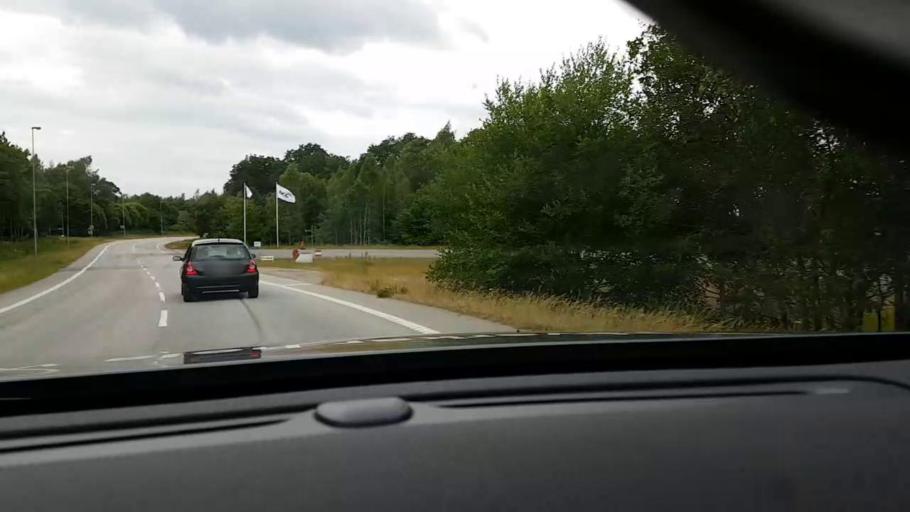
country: SE
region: Skane
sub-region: Hassleholms Kommun
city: Hassleholm
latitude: 56.1723
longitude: 13.7697
